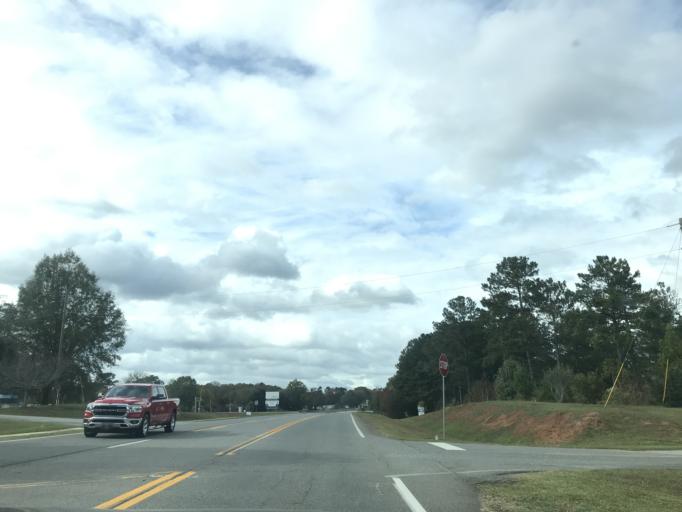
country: US
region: Georgia
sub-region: Jones County
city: Gray
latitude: 32.9990
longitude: -83.5292
